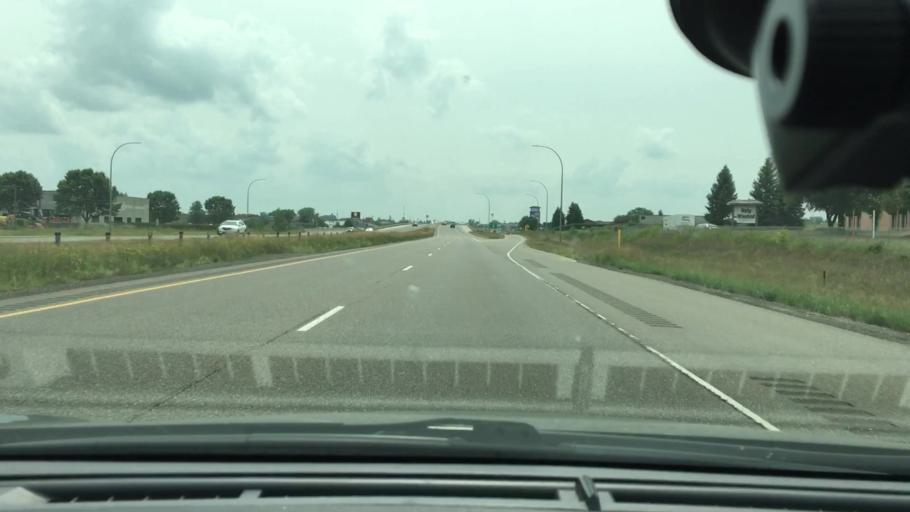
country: US
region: Minnesota
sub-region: Hennepin County
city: Rogers
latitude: 45.2154
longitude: -93.5528
